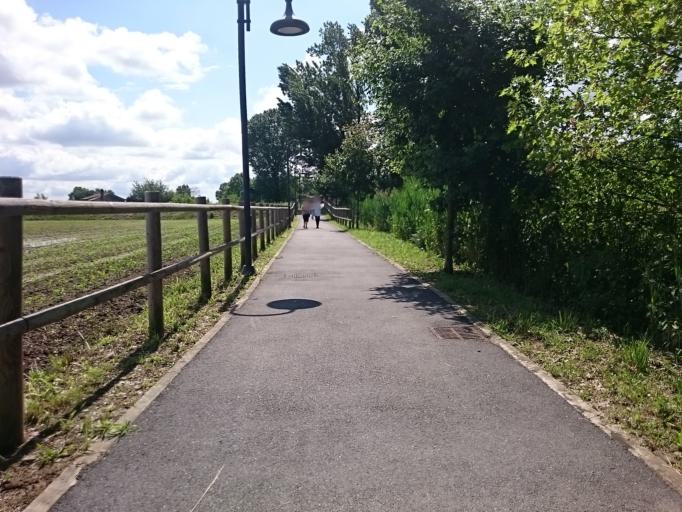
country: IT
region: Veneto
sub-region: Provincia di Padova
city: Arlesega
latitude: 45.4631
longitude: 11.7210
